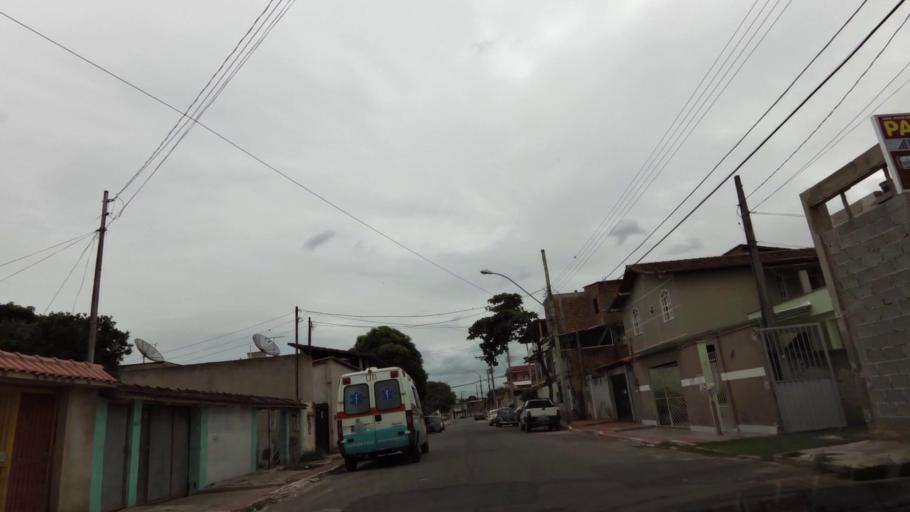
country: BR
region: Espirito Santo
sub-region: Guarapari
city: Guarapari
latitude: -20.6651
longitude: -40.5090
